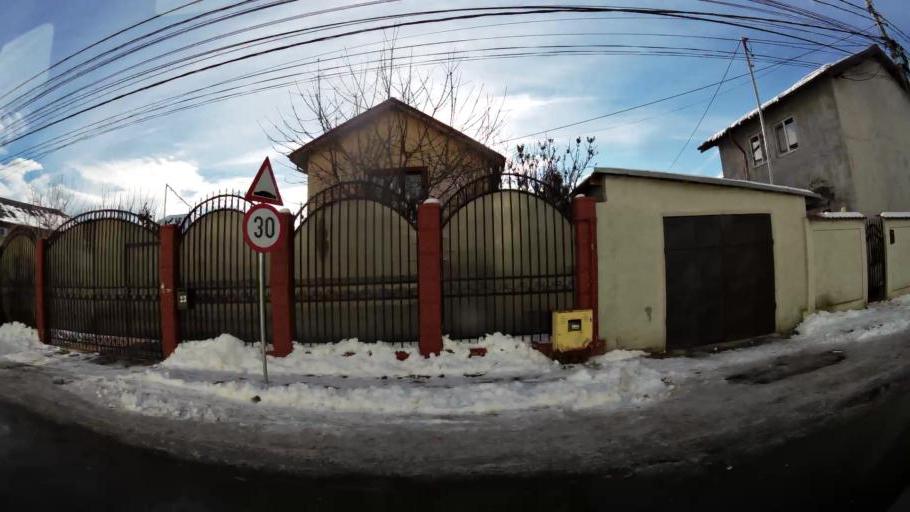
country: RO
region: Ilfov
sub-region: Voluntari City
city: Voluntari
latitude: 44.4926
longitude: 26.1975
